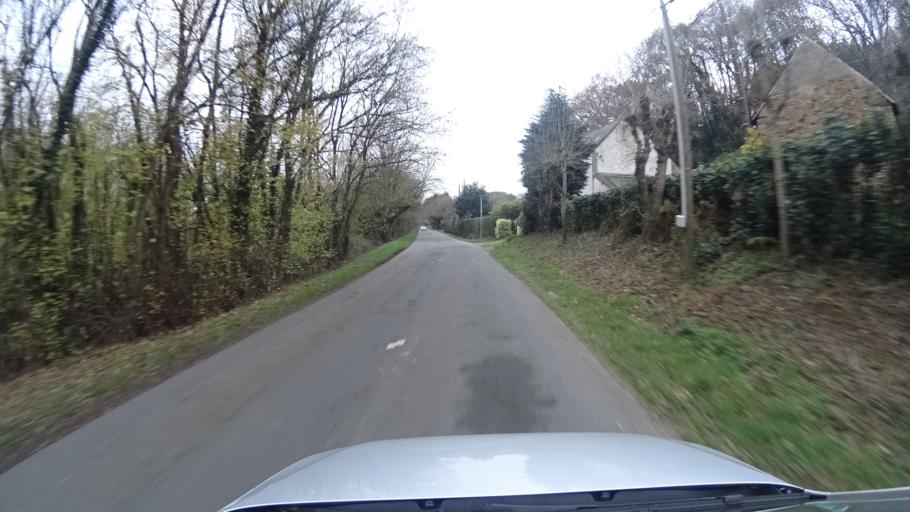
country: FR
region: Brittany
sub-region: Departement d'Ille-et-Vilaine
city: Langon
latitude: 47.7025
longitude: -1.8798
